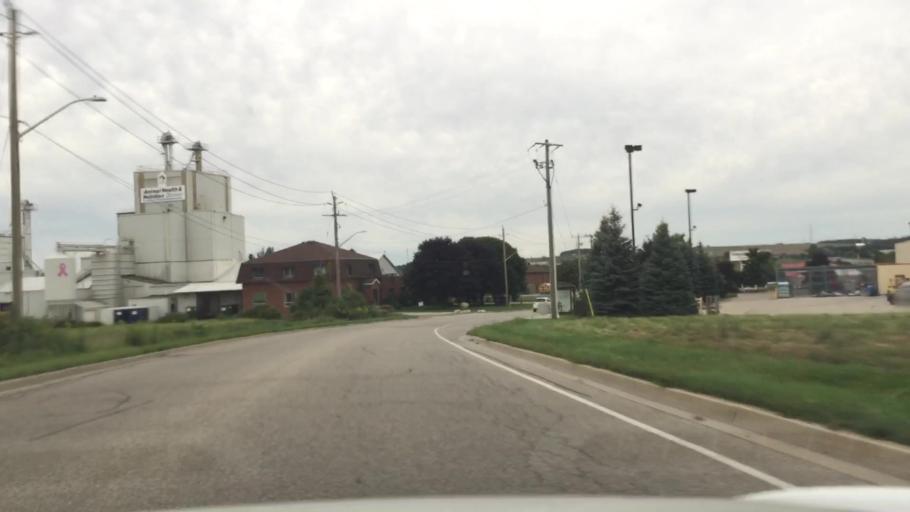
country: CA
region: Ontario
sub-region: Oxford County
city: Woodstock
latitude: 43.1148
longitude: -80.7319
